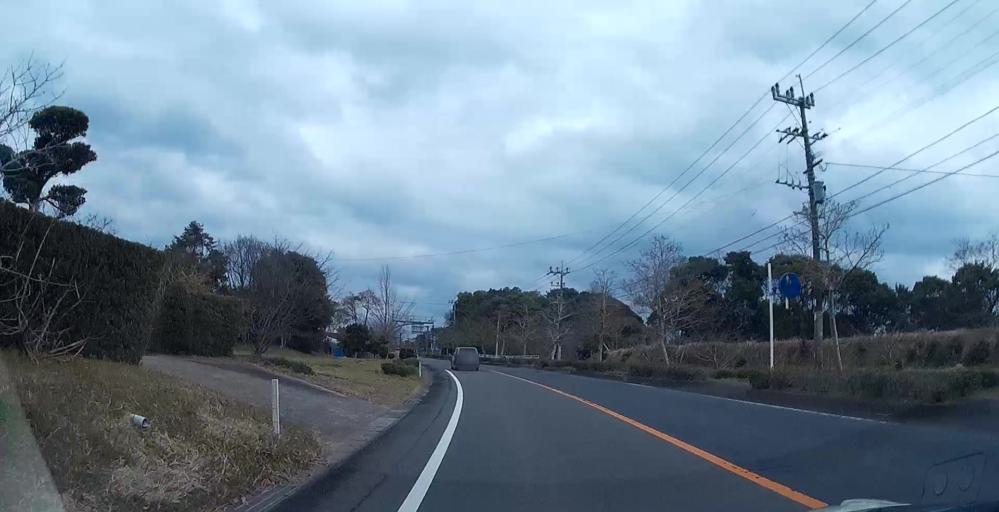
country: JP
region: Kagoshima
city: Akune
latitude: 32.0778
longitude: 130.2055
